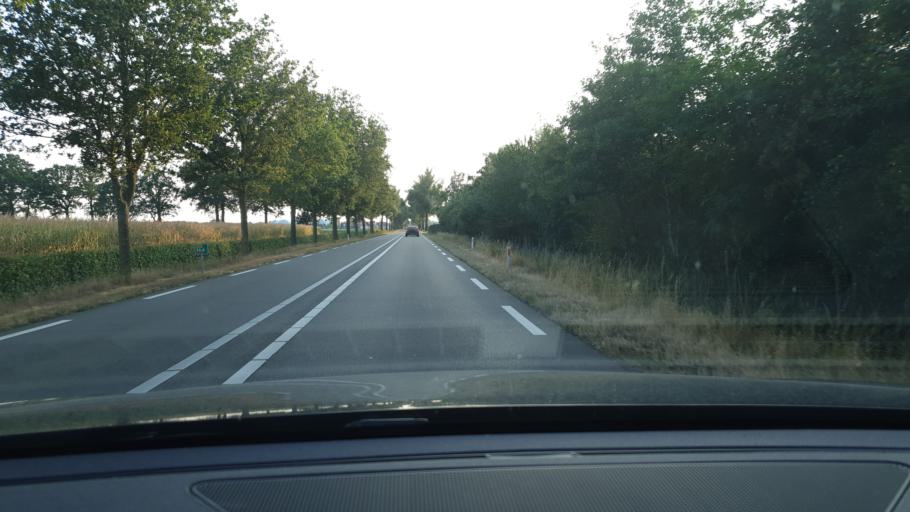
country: NL
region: North Brabant
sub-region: Gemeente Mill en Sint Hubert
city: Wilbertoord
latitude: 51.6674
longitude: 5.7566
